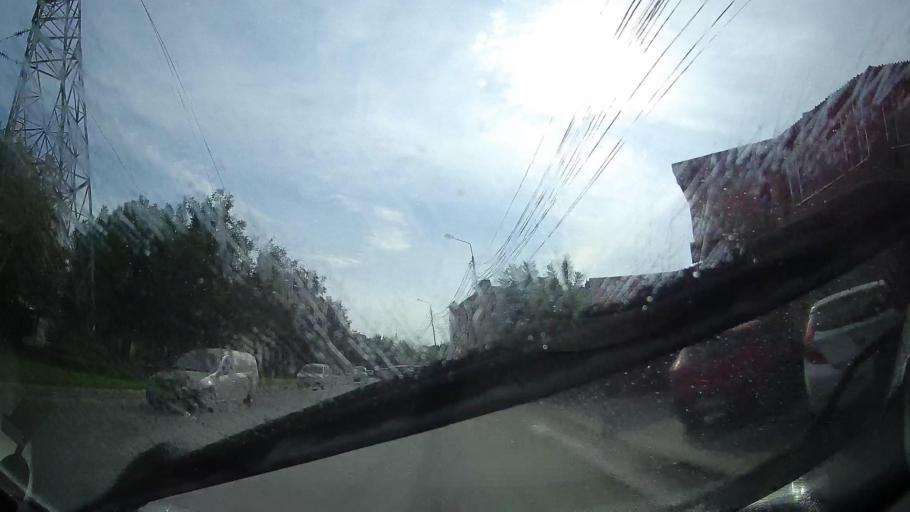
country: RU
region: Rostov
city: Severnyy
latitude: 47.2708
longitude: 39.7058
